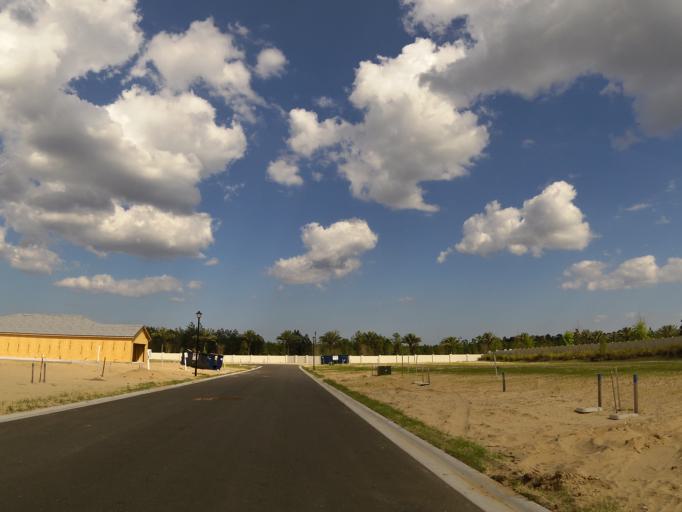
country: US
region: Florida
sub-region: Saint Johns County
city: Palm Valley
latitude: 30.1711
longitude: -81.5082
